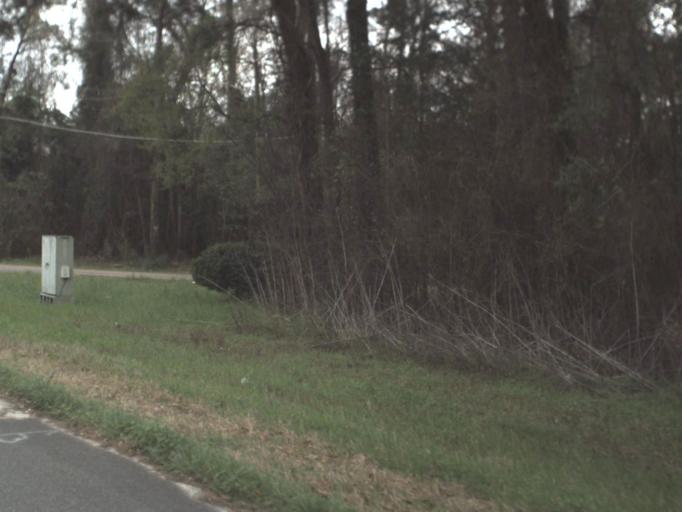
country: US
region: Florida
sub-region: Leon County
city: Tallahassee
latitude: 30.5043
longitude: -84.3306
